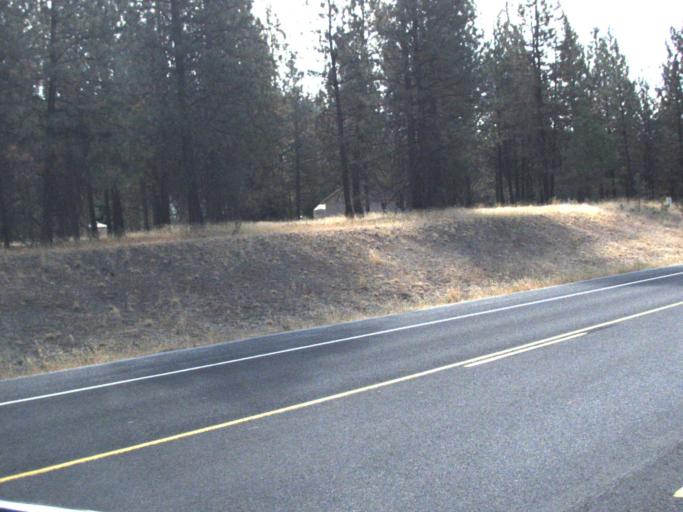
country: US
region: Washington
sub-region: Spokane County
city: Town and Country
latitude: 47.7431
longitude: -117.5075
